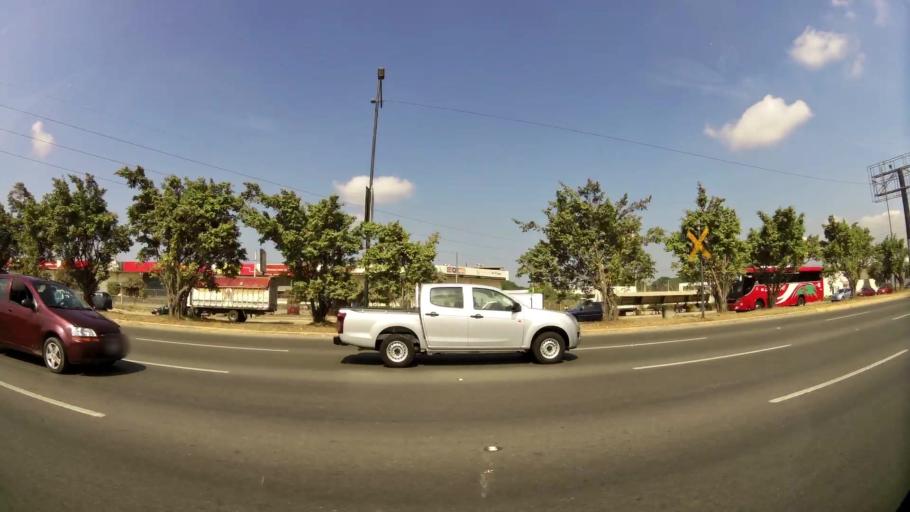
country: EC
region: Guayas
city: Eloy Alfaro
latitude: -2.1778
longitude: -79.8266
